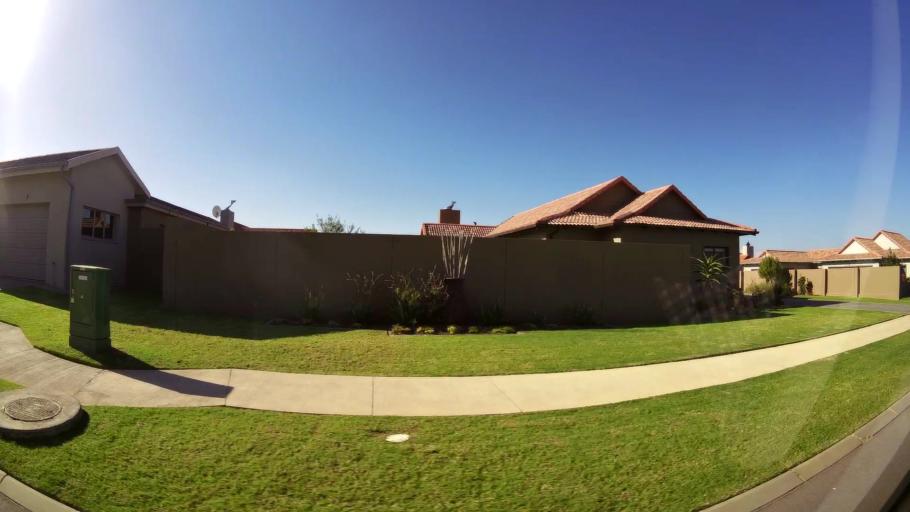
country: ZA
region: Western Cape
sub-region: Eden District Municipality
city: George
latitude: -33.9609
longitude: 22.4227
